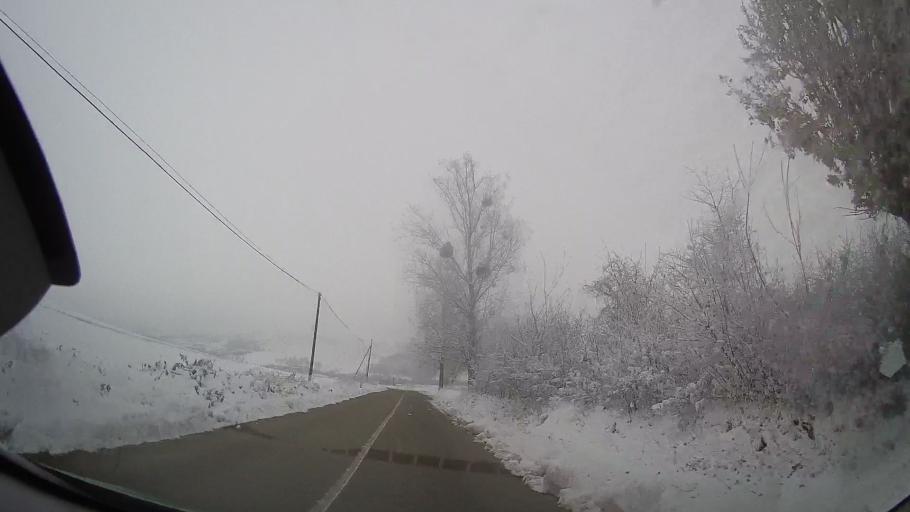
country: RO
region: Neamt
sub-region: Comuna Bozieni
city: Bozieni
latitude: 46.8447
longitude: 27.1687
